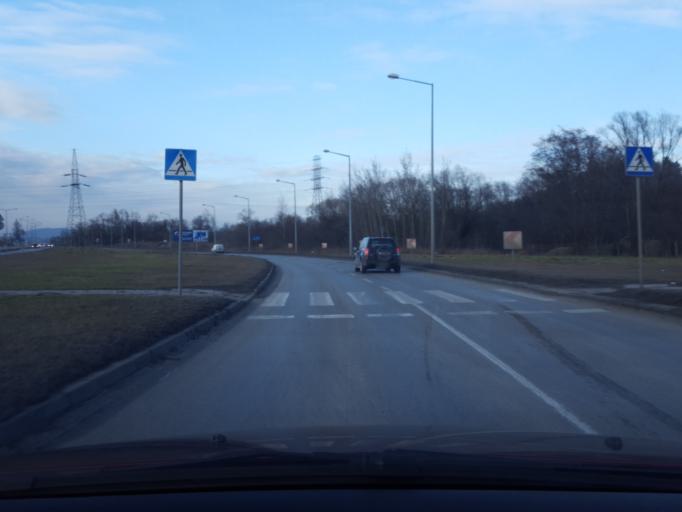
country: PL
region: Lesser Poland Voivodeship
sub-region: Powiat nowosadecki
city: Nawojowa
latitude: 49.5931
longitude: 20.7328
